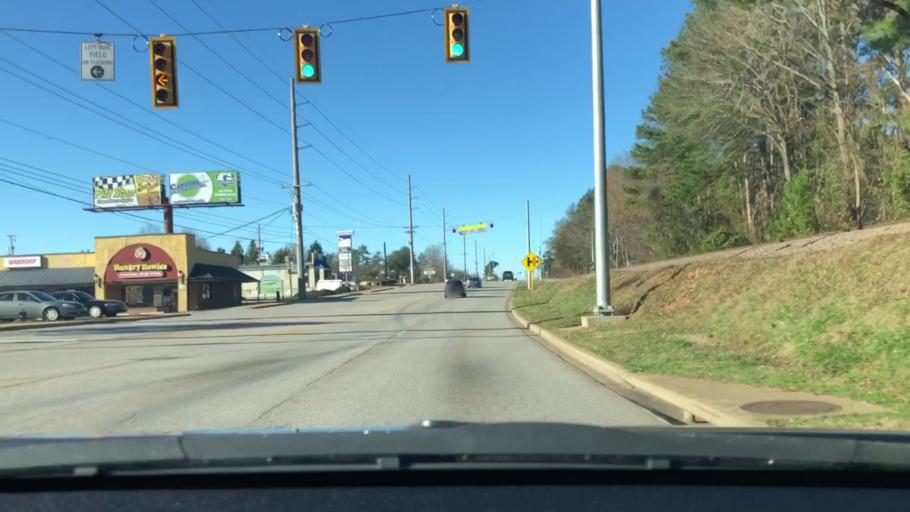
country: US
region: South Carolina
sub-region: Lexington County
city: Irmo
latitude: 34.0716
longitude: -81.1750
